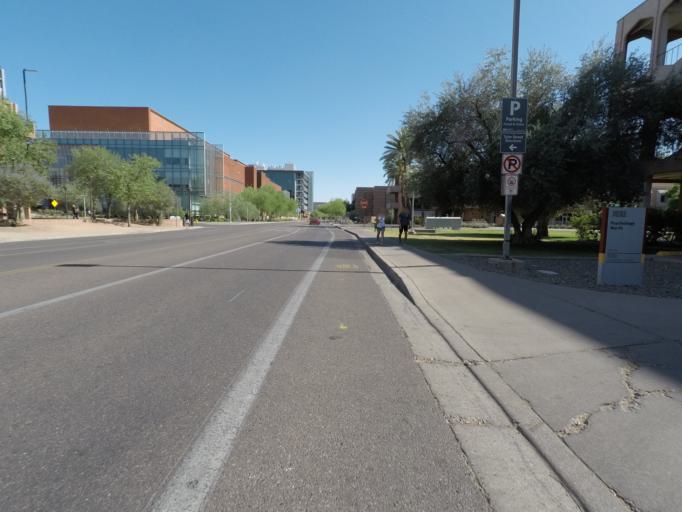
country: US
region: Arizona
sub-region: Maricopa County
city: Tempe Junction
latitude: 33.4207
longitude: -111.9290
